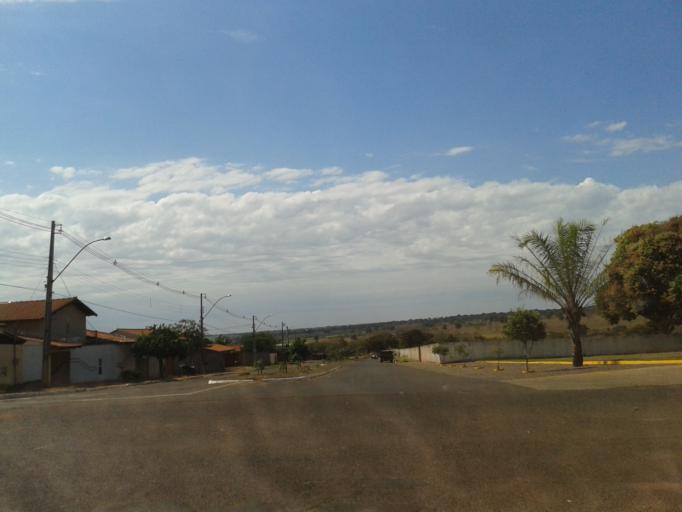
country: BR
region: Minas Gerais
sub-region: Santa Vitoria
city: Santa Vitoria
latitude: -18.8420
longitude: -50.1176
